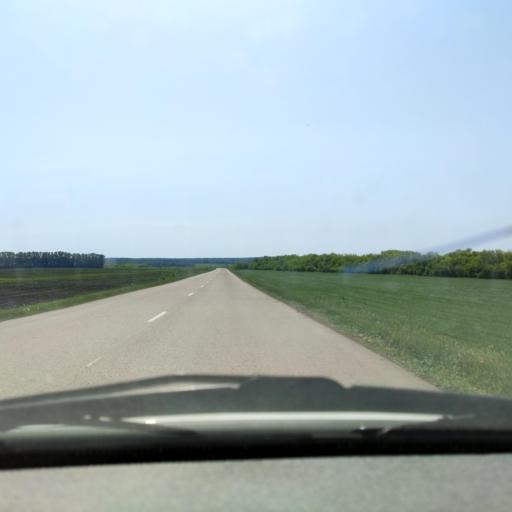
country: RU
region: Bashkortostan
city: Avdon
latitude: 54.5460
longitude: 55.6522
